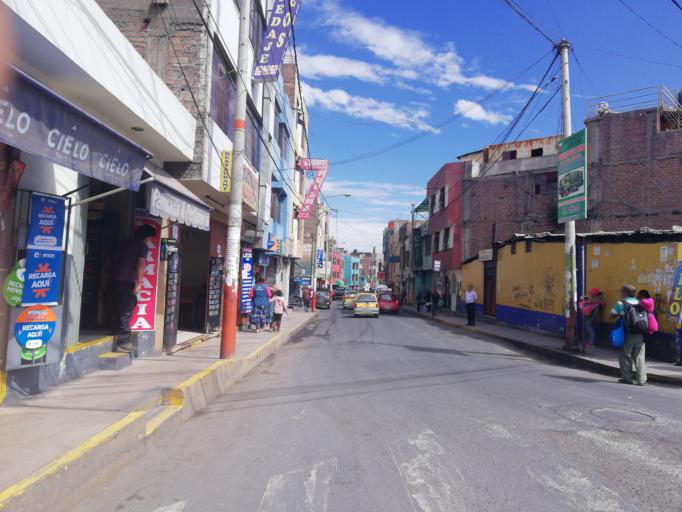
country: PE
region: Arequipa
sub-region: Provincia de Arequipa
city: Arequipa
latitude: -16.4230
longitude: -71.5424
